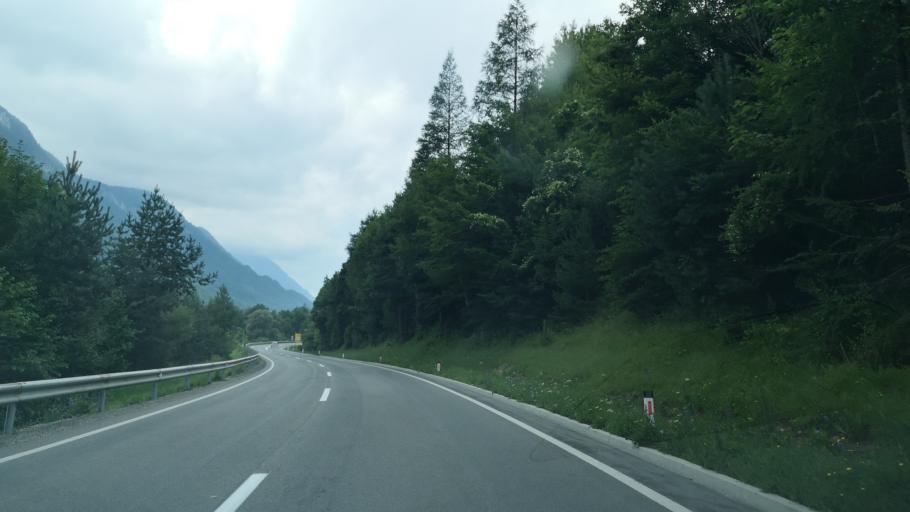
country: SI
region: Jesenice
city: Hrusica
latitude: 46.4446
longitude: 14.0301
